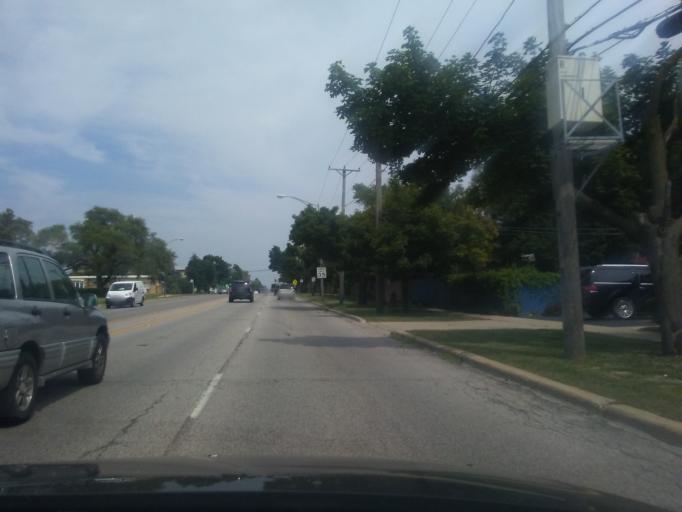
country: US
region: Illinois
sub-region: Cook County
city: Norridge
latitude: 41.9667
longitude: -87.8300
